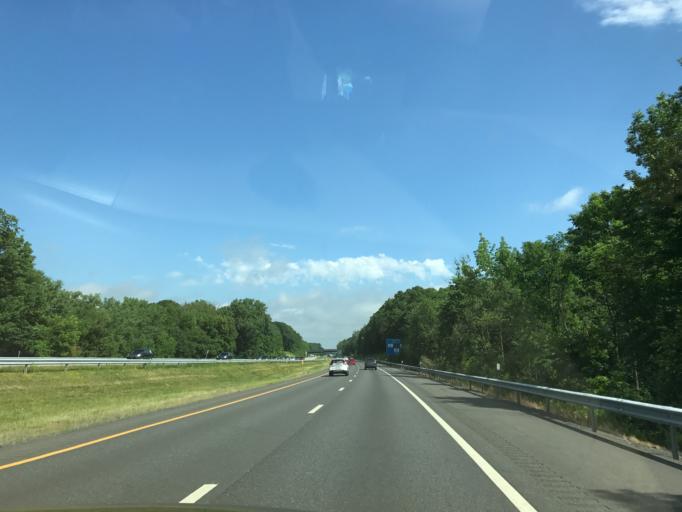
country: US
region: New York
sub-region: Orange County
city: Gardnertown
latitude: 41.5565
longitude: -74.0807
